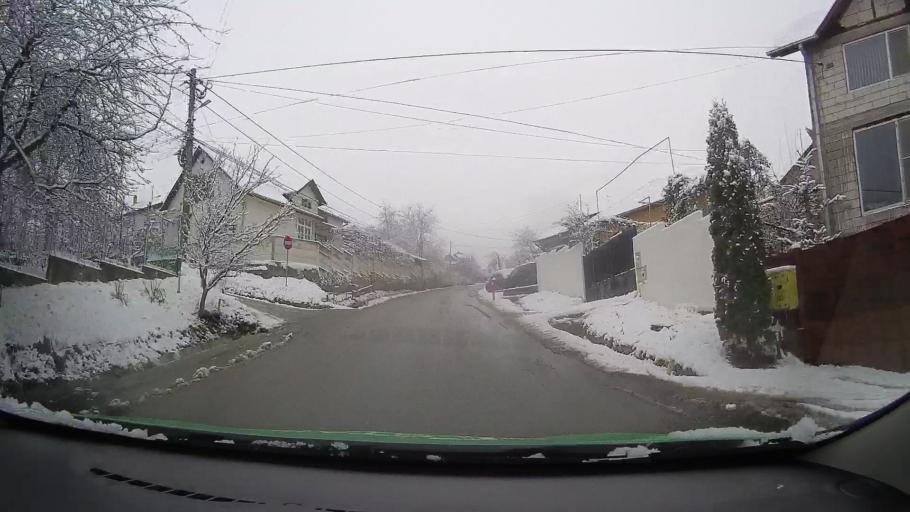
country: RO
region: Hunedoara
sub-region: Municipiul Deva
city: Deva
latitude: 45.8711
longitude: 22.8967
